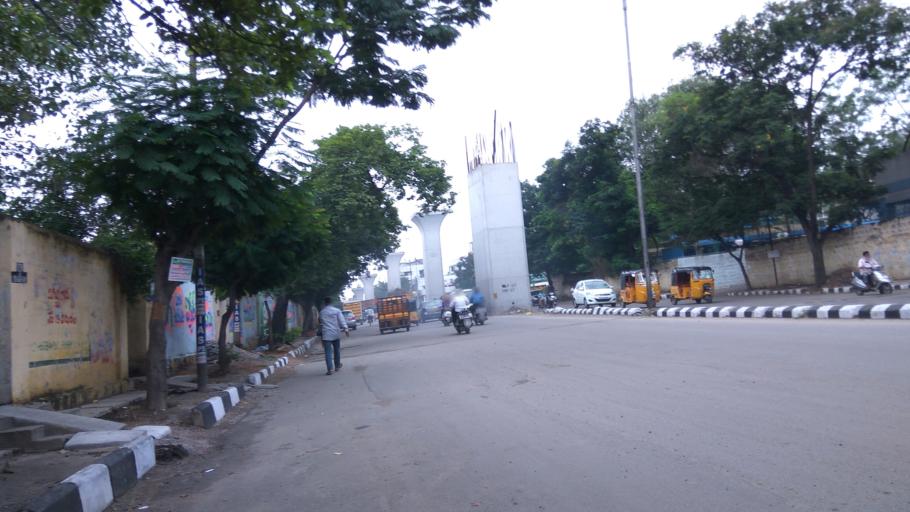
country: IN
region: Telangana
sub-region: Hyderabad
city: Malkajgiri
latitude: 17.4324
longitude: 78.5060
